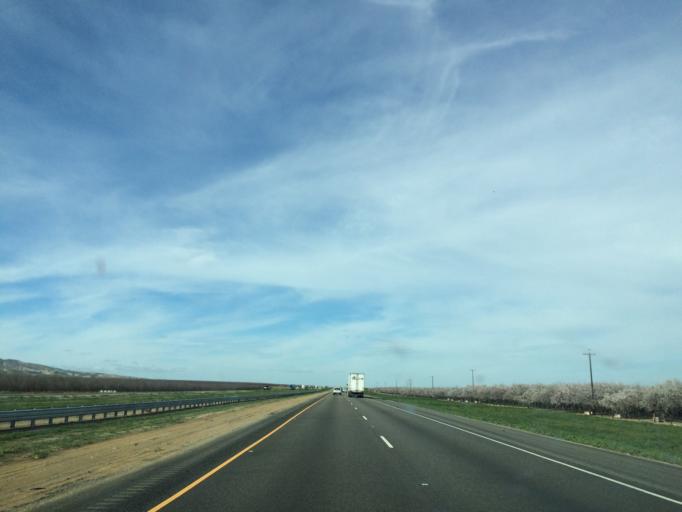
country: US
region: California
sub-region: Fresno County
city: Firebaugh
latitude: 36.6917
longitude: -120.6626
